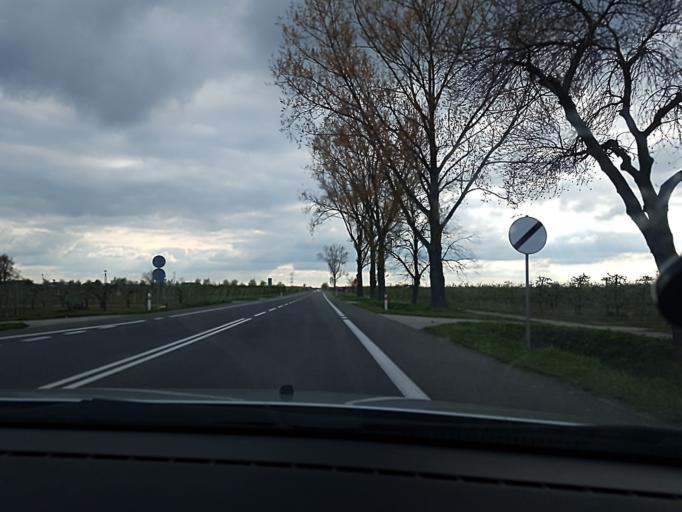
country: PL
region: Lodz Voivodeship
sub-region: powiat Lowicki
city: Bobrowniki
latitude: 52.1267
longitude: 20.0154
